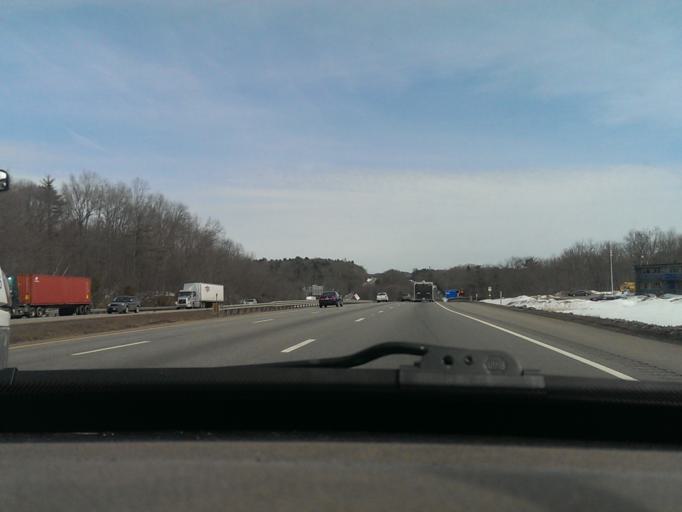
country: US
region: Massachusetts
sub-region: Worcester County
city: Sturbridge
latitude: 42.1348
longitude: -72.0429
